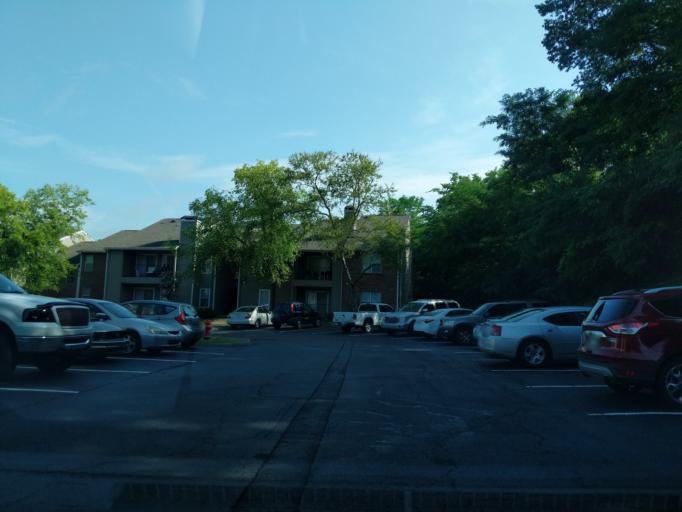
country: US
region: Tennessee
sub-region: Sumner County
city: Hendersonville
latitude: 36.3108
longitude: -86.6515
